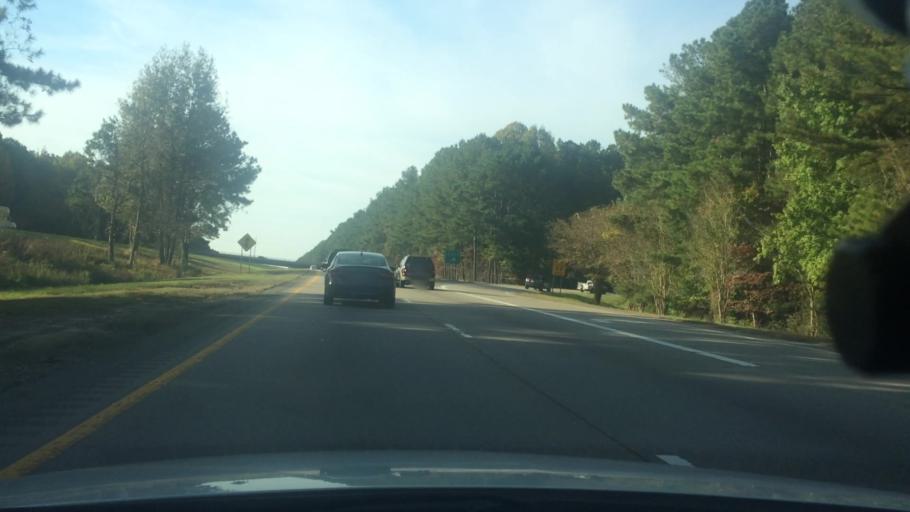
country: US
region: North Carolina
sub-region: Wake County
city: Cary
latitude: 35.8179
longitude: -78.7387
